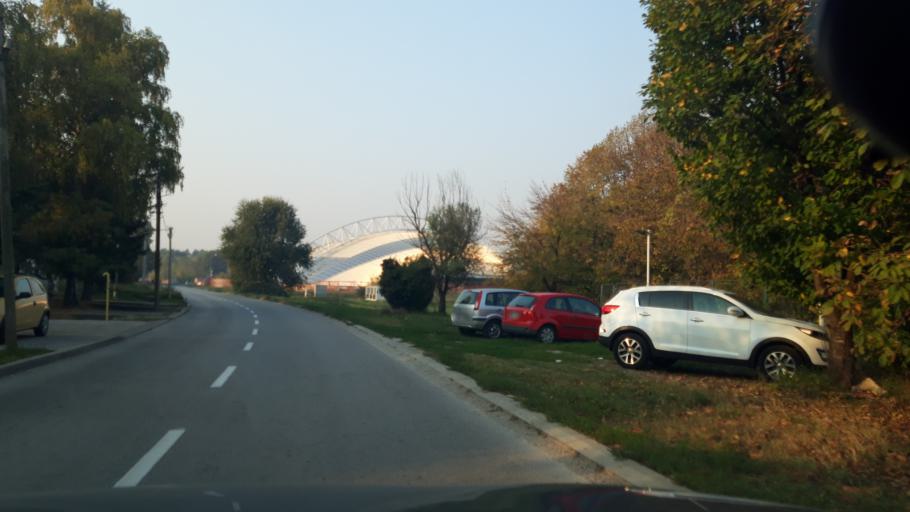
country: RS
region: Autonomna Pokrajina Vojvodina
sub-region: Sremski Okrug
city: Ingija
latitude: 45.0520
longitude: 20.0672
